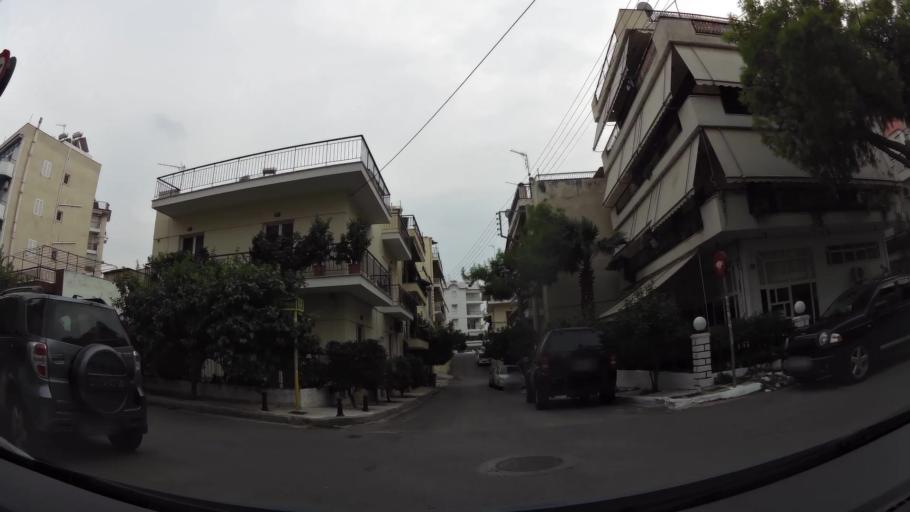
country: GR
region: Attica
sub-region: Nomarchia Athinas
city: Alimos
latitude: 37.9194
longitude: 23.7317
